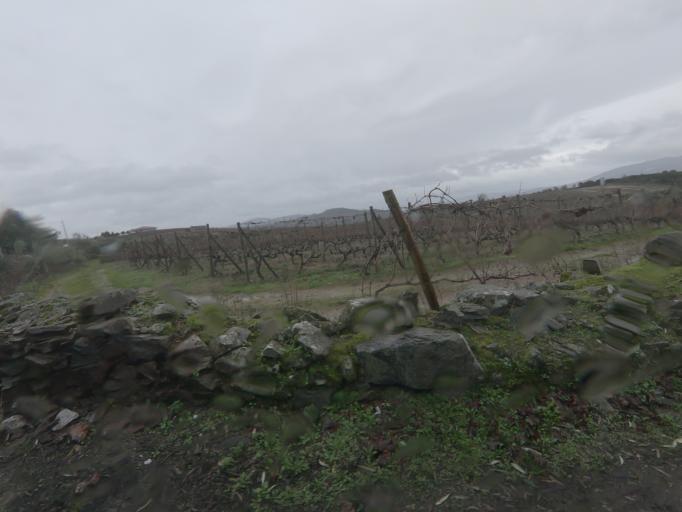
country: PT
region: Viseu
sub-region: Armamar
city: Armamar
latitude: 41.1672
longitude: -7.7157
